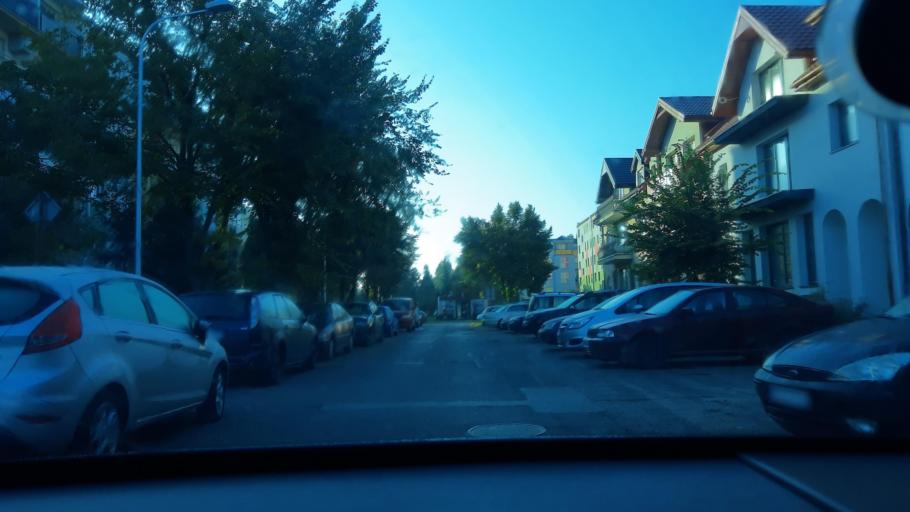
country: PL
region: Lodz Voivodeship
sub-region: Powiat sieradzki
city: Sieradz
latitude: 51.5930
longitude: 18.7106
